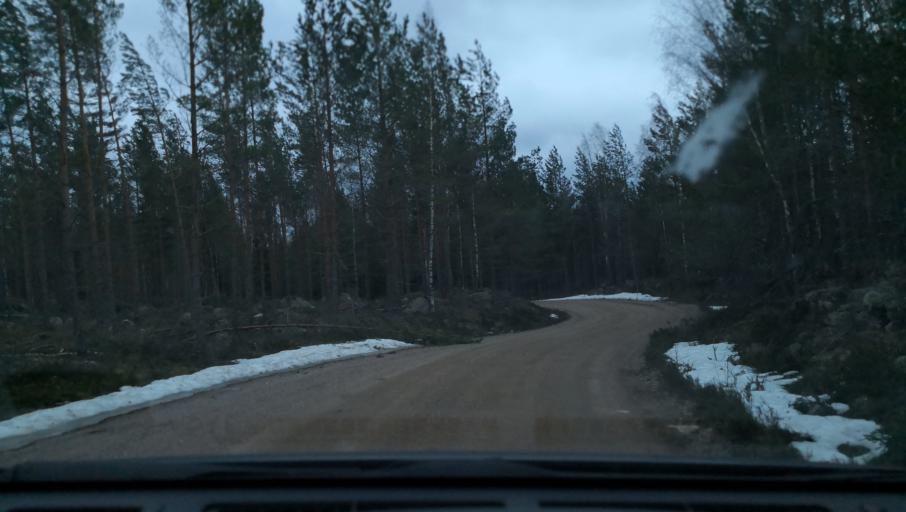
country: SE
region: OErebro
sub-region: Lindesbergs Kommun
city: Fellingsbro
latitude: 59.6086
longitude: 15.5763
